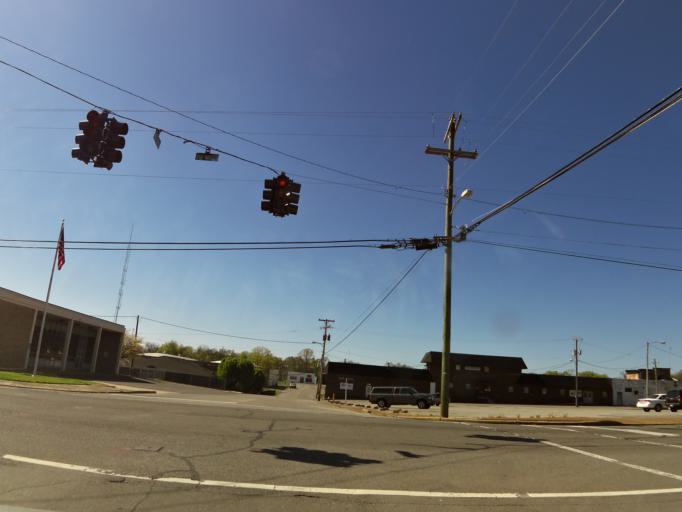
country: US
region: Tennessee
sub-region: Robertson County
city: Springfield
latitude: 36.5070
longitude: -86.8842
